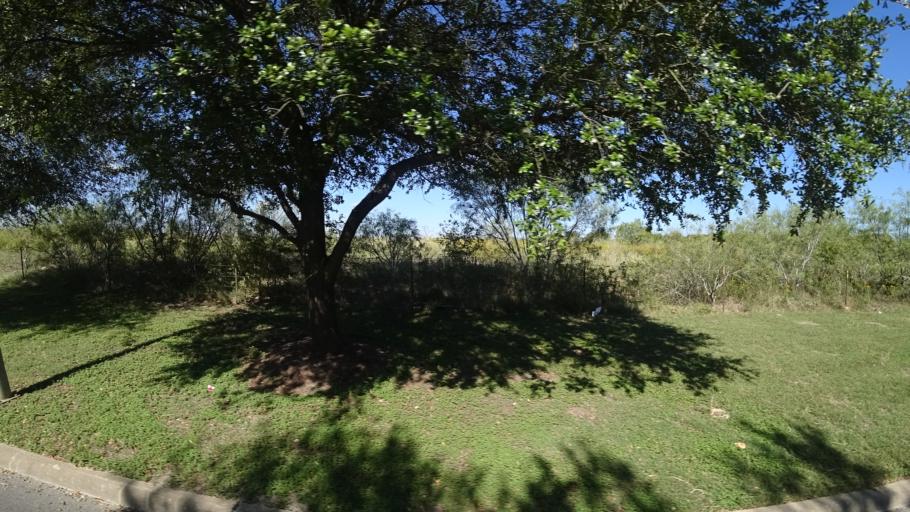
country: US
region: Texas
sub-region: Travis County
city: Manor
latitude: 30.3386
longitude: -97.6098
